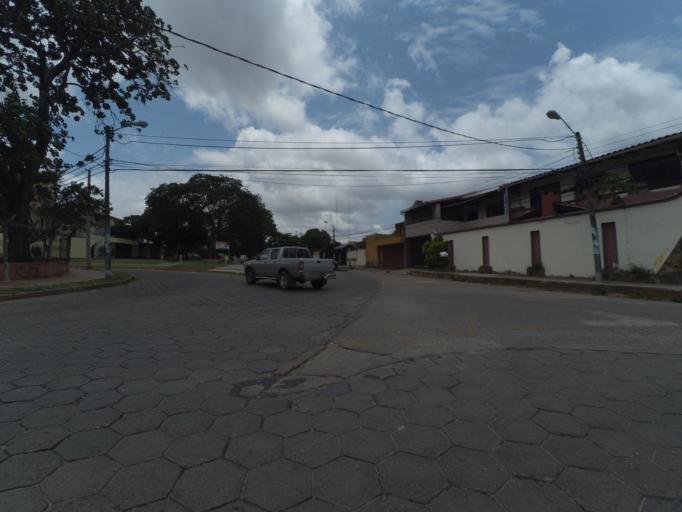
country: BO
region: Santa Cruz
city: Santa Cruz de la Sierra
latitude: -17.7986
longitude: -63.2007
